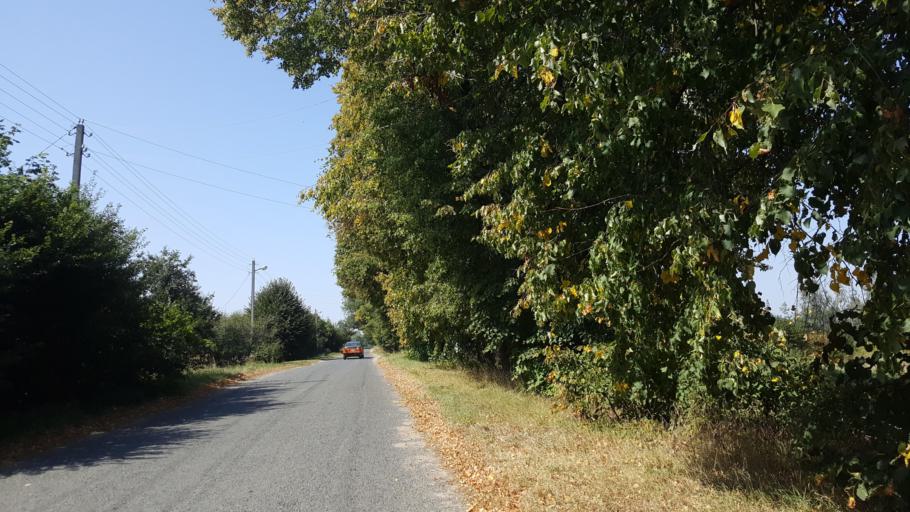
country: BY
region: Brest
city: Vysokaye
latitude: 52.4478
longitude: 23.4570
